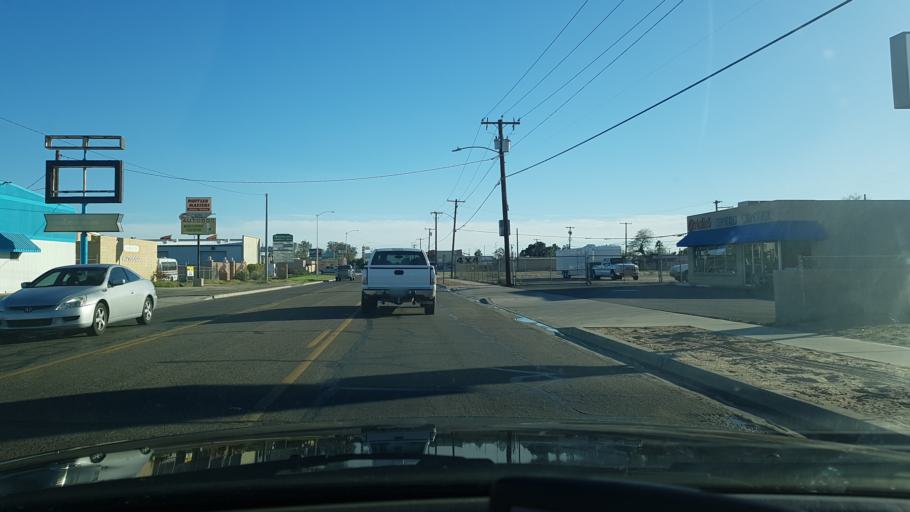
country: US
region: Arizona
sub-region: Yuma County
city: Yuma
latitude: 32.6940
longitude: -114.6160
